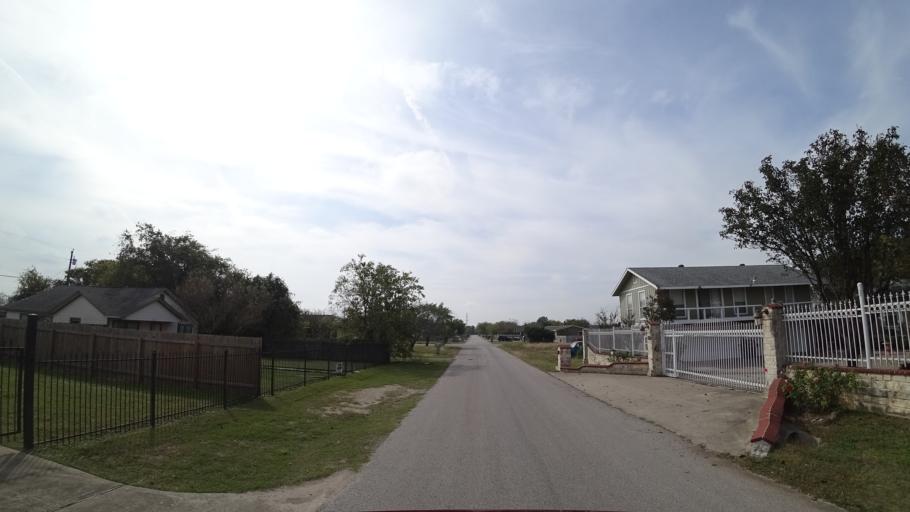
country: US
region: Texas
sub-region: Travis County
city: Wells Branch
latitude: 30.4521
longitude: -97.6693
